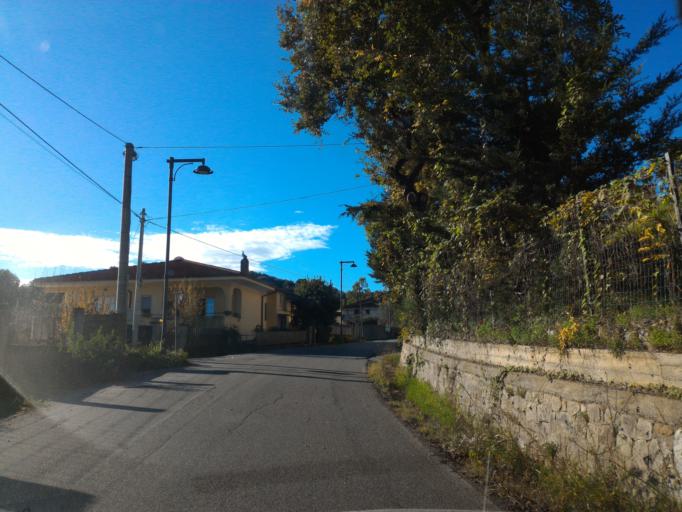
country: IT
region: Calabria
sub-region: Provincia di Crotone
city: Torretta
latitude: 39.4448
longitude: 17.0382
